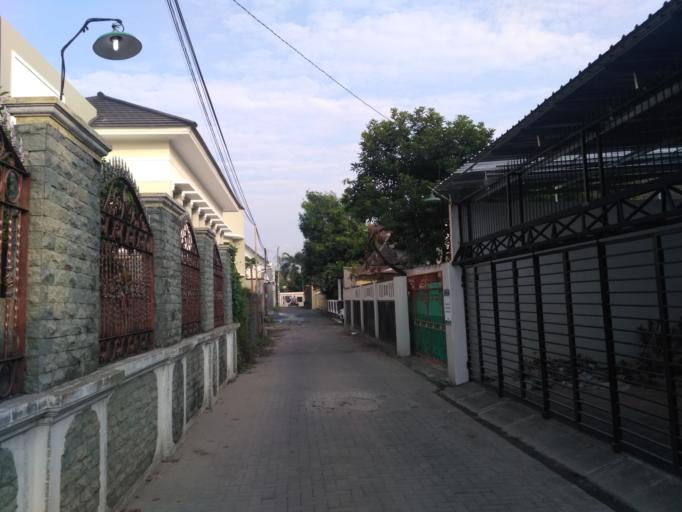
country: ID
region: Daerah Istimewa Yogyakarta
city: Melati
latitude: -7.7524
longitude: 110.3815
